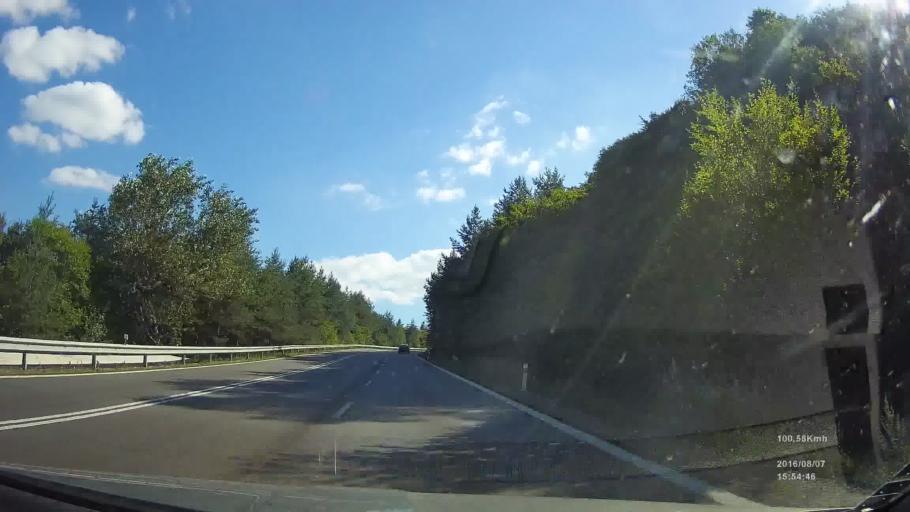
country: SK
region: Presovsky
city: Giraltovce
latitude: 49.0833
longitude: 21.4436
